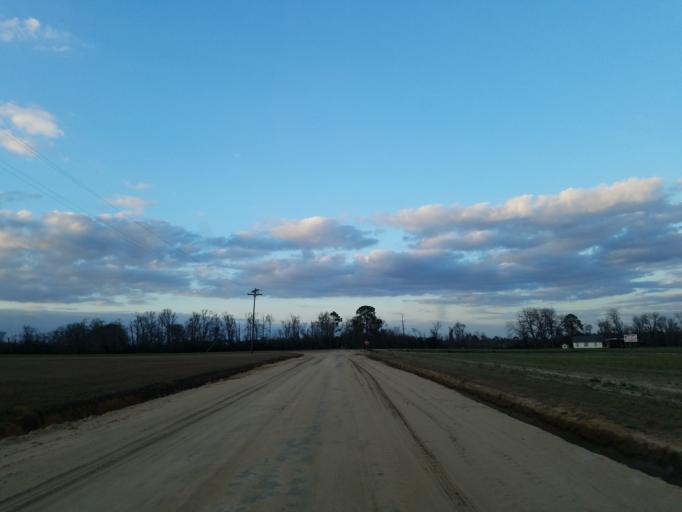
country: US
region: Georgia
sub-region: Dooly County
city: Vienna
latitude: 32.0916
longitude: -83.7520
